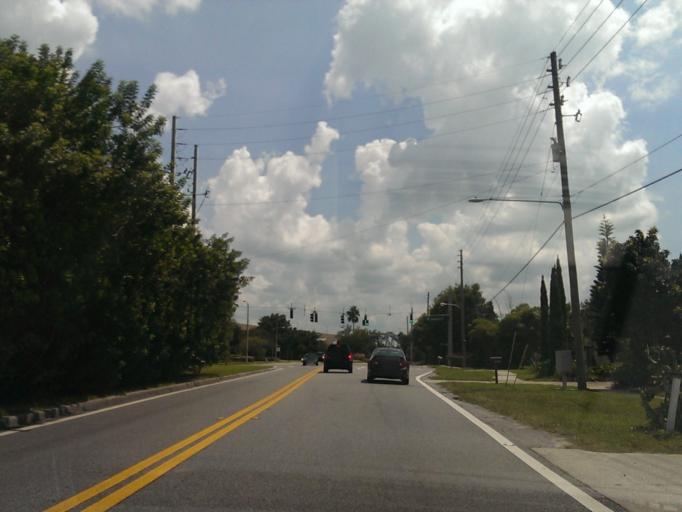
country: US
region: Florida
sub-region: Orange County
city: Doctor Phillips
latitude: 28.4811
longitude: -81.4756
